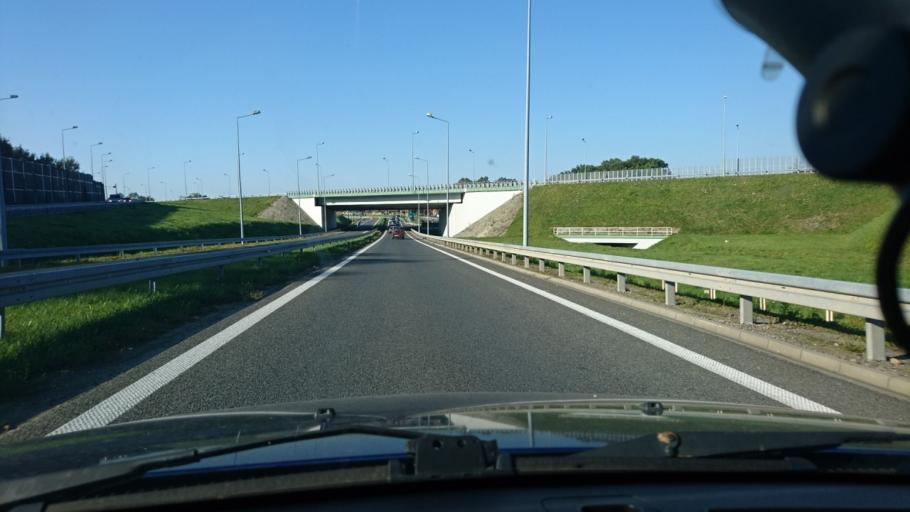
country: PL
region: Silesian Voivodeship
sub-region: Bielsko-Biala
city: Bielsko-Biala
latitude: 49.8436
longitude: 19.0687
